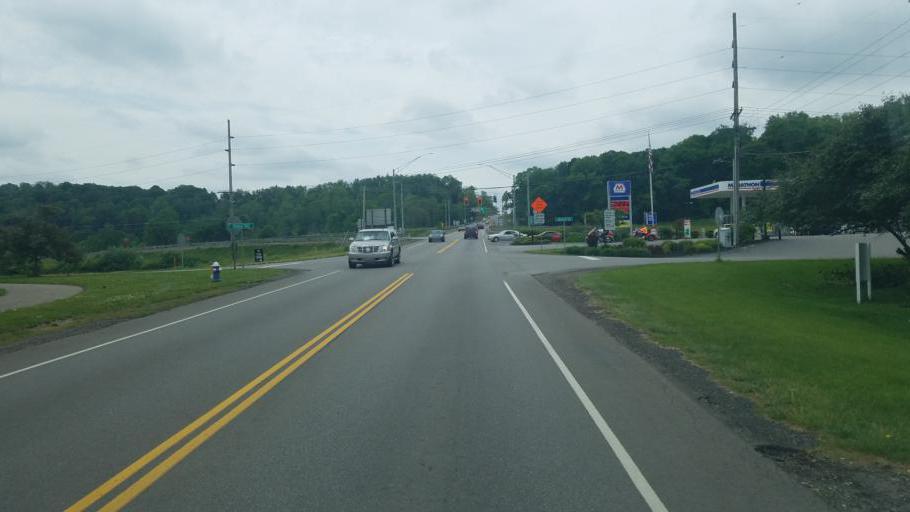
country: US
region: Ohio
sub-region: Licking County
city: Granville
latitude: 40.0605
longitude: -82.5208
